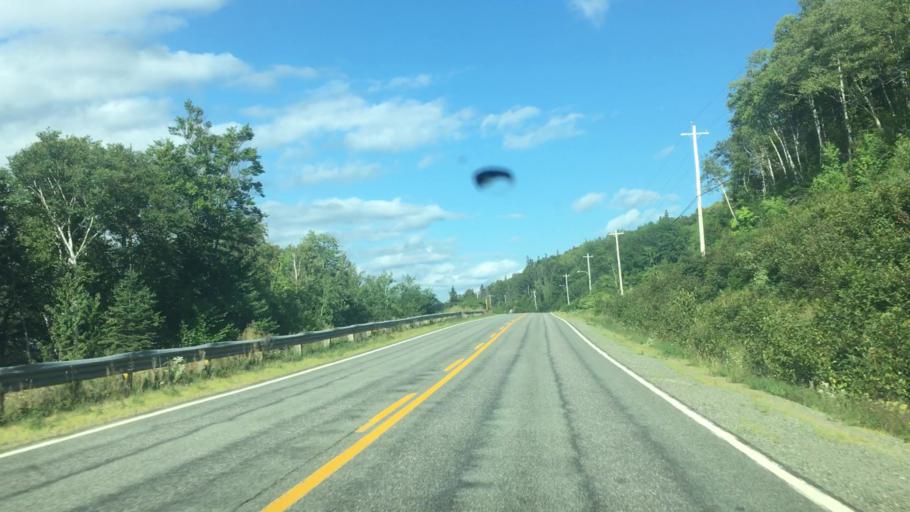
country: CA
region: Nova Scotia
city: Sydney
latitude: 45.8703
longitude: -60.6092
